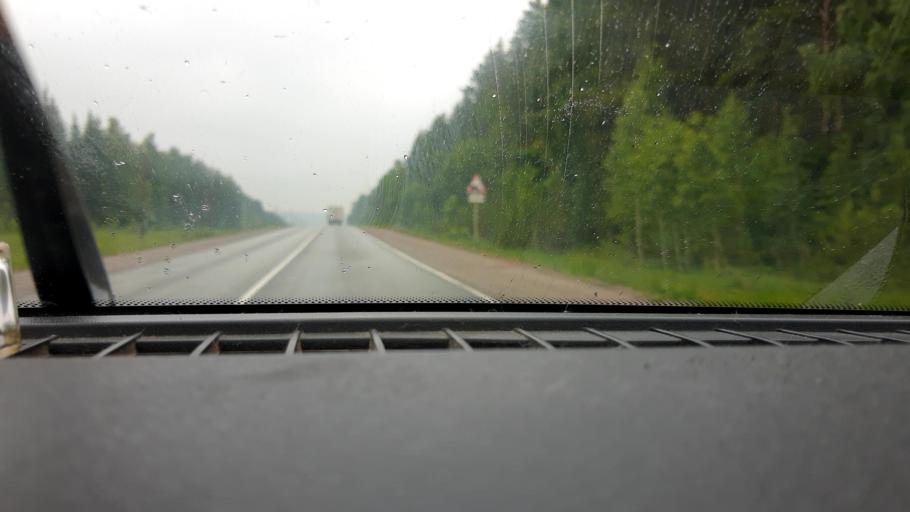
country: RU
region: Bashkortostan
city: Belebey
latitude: 54.2179
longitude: 54.0759
